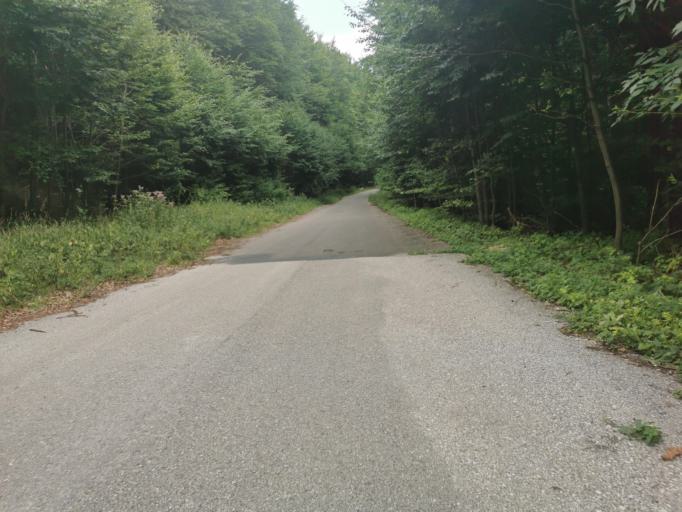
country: CZ
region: South Moravian
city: Velka nad Velickou
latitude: 48.8464
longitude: 17.6106
